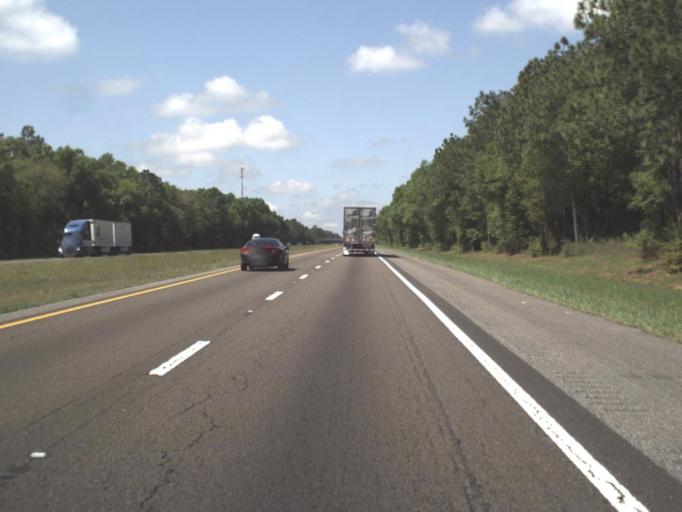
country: US
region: Florida
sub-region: Santa Rosa County
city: East Milton
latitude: 30.6605
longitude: -86.8691
